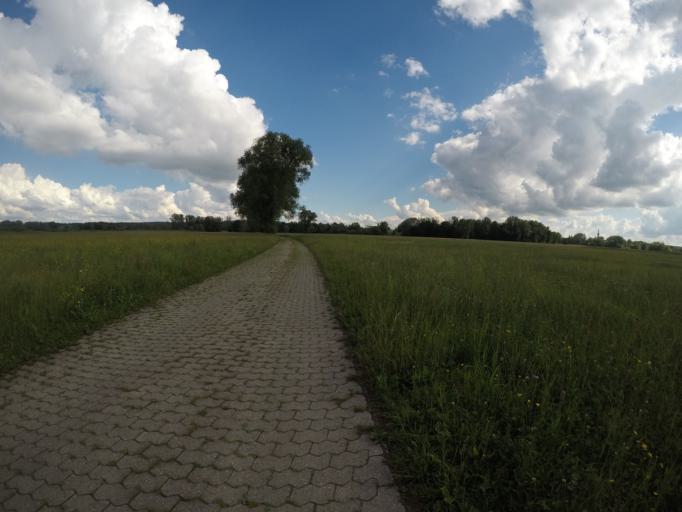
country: DE
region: Bavaria
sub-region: Lower Bavaria
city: Marklkofen
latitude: 48.5628
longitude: 12.5617
